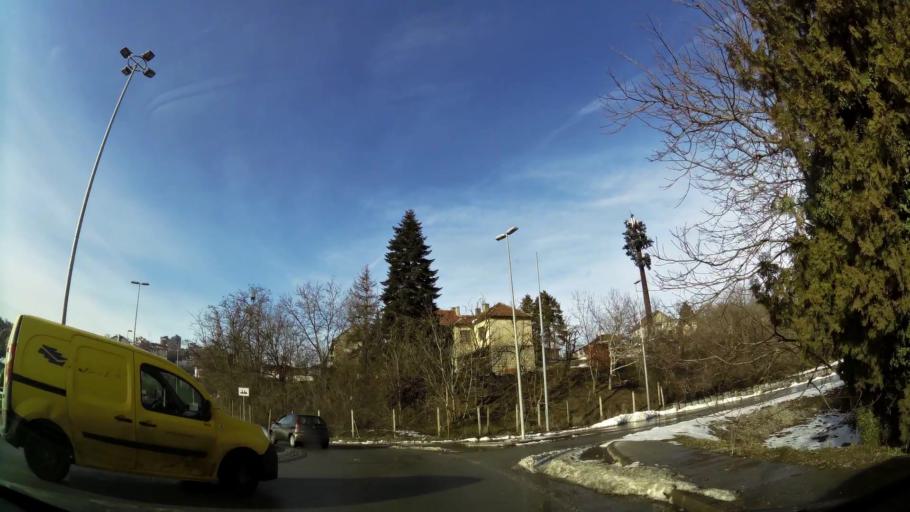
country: RS
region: Central Serbia
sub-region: Belgrade
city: Rakovica
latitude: 44.7319
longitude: 20.4328
